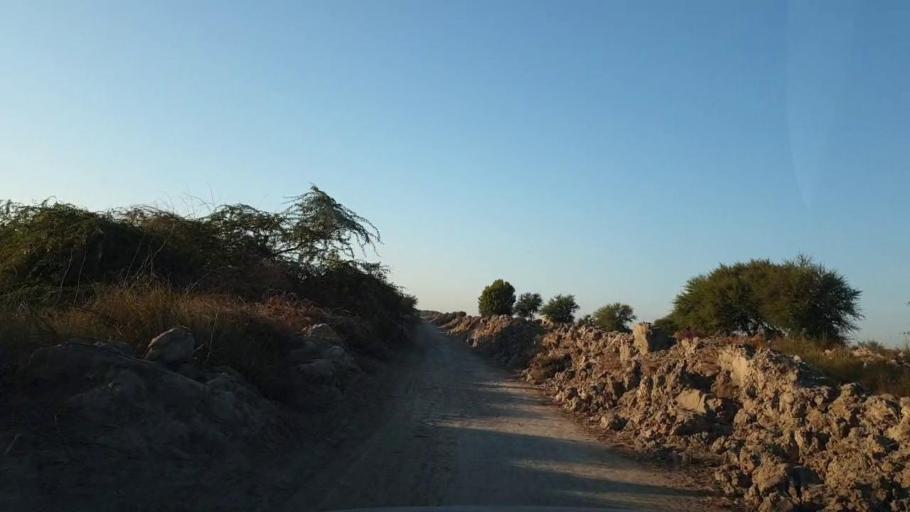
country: PK
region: Sindh
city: Jhol
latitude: 25.8886
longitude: 68.8954
